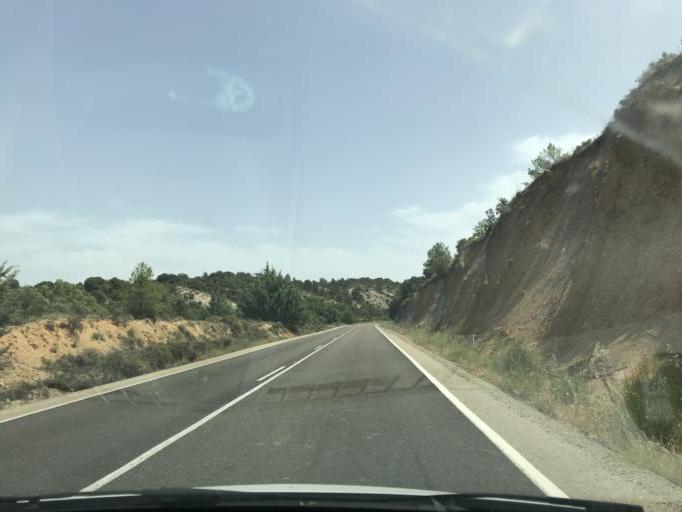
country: ES
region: Castille-La Mancha
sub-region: Provincia de Cuenca
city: La Frontera
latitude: 40.4012
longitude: -2.2485
